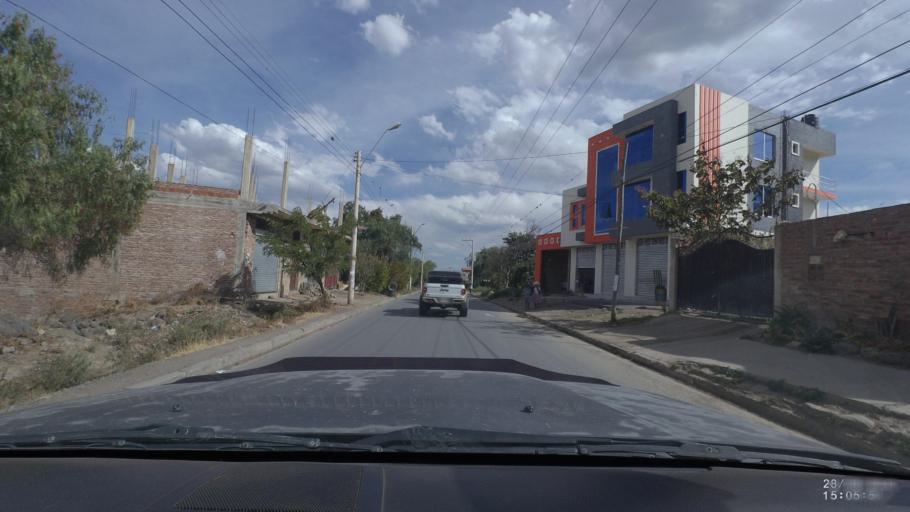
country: BO
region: Cochabamba
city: Cochabamba
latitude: -17.3345
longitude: -66.2837
